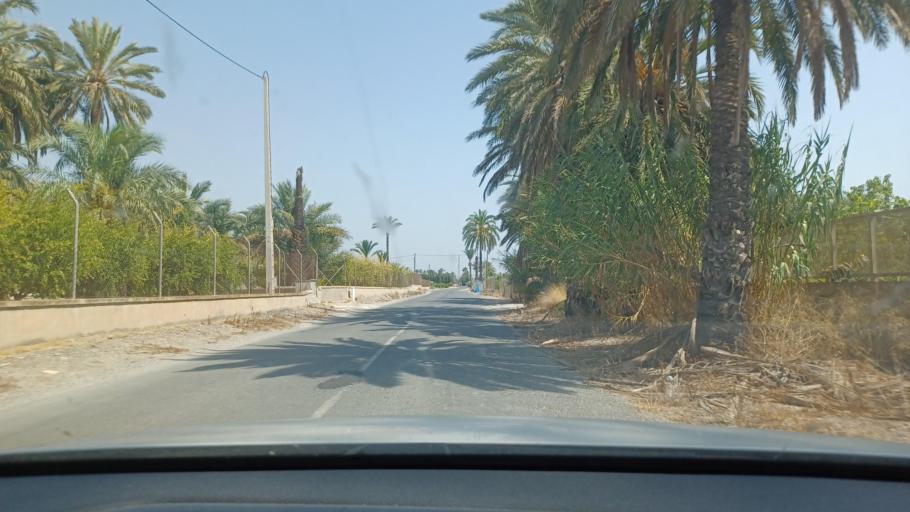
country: ES
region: Valencia
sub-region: Provincia de Alicante
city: Elche
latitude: 38.2248
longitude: -0.6949
